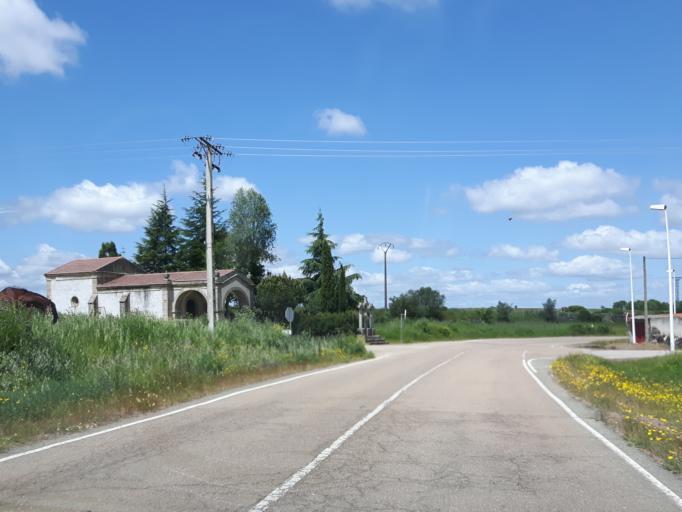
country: ES
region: Castille and Leon
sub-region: Provincia de Salamanca
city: Villar de la Yegua
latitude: 40.7237
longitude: -6.7051
